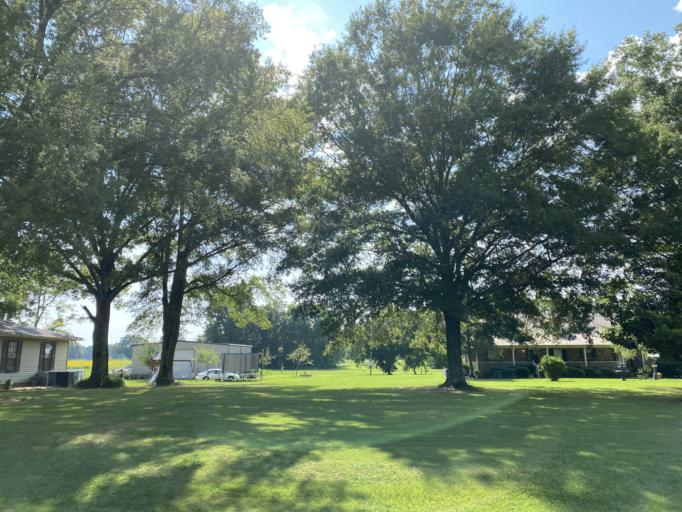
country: US
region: Alabama
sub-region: Lawrence County
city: Town Creek
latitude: 34.6671
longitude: -87.4060
